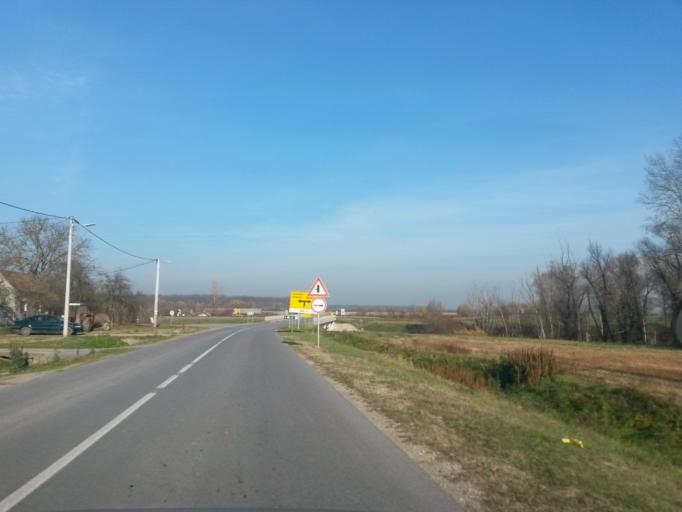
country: HR
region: Vukovarsko-Srijemska
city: Privlaka
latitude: 45.2115
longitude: 18.8574
